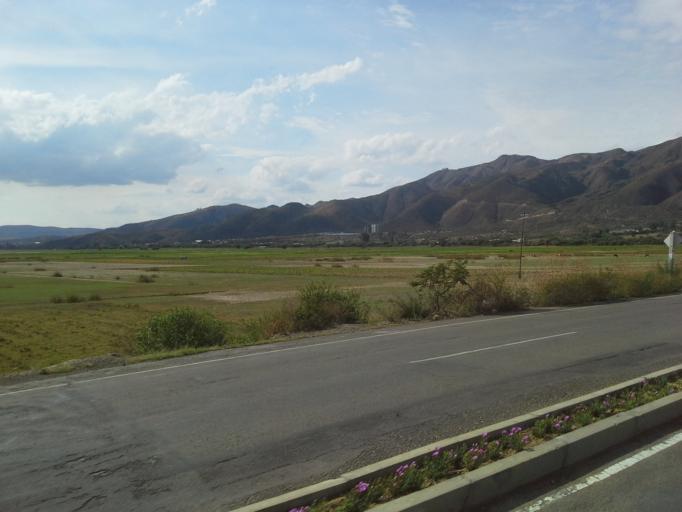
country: BO
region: Cochabamba
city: Tarata
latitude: -17.5554
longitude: -66.0077
